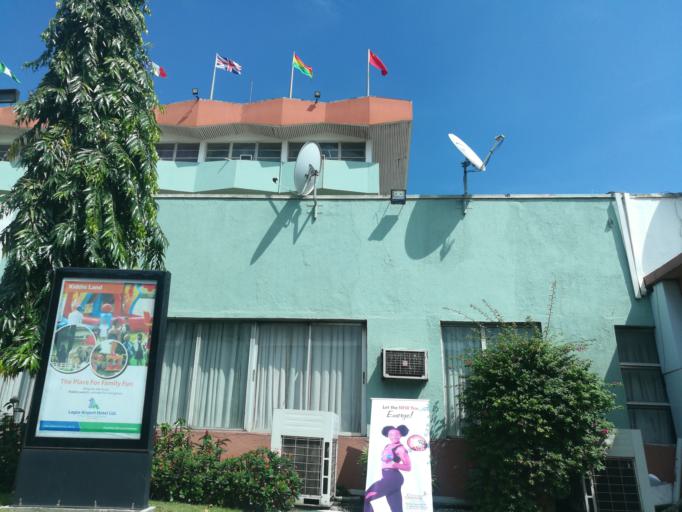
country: NG
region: Lagos
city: Ikeja
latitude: 6.6065
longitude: 3.3467
